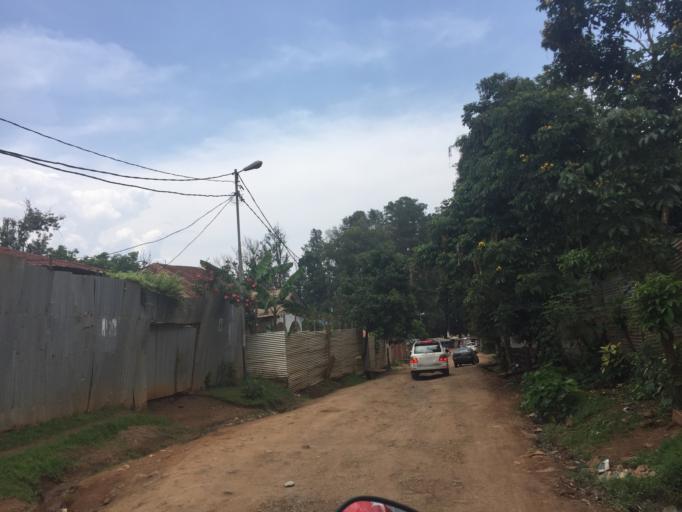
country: CD
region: South Kivu
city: Bukavu
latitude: -2.4855
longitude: 28.8588
